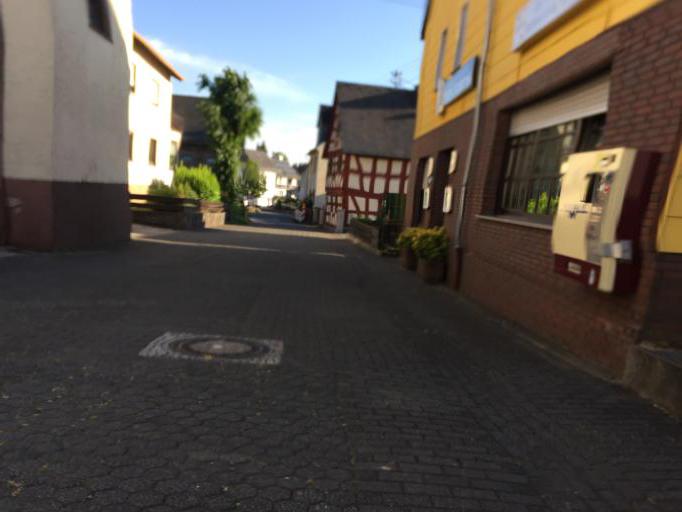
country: DE
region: Rheinland-Pfalz
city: Berod bei Wallmerod
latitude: 50.4824
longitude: 7.9352
